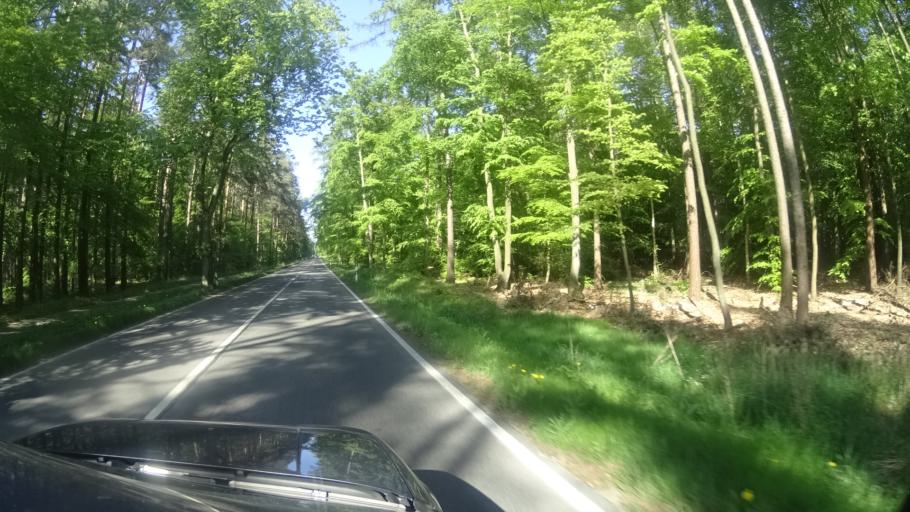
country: DE
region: Mecklenburg-Vorpommern
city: Rovershagen
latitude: 54.2167
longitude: 12.2153
